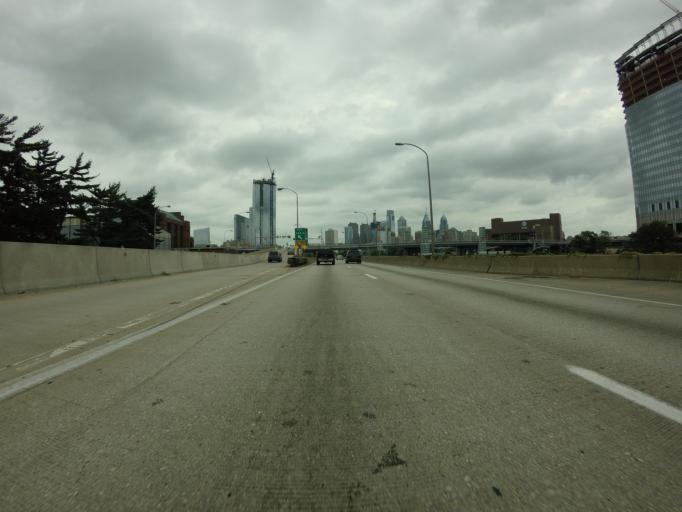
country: US
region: Pennsylvania
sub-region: Philadelphia County
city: Philadelphia
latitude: 39.9464
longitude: -75.1890
